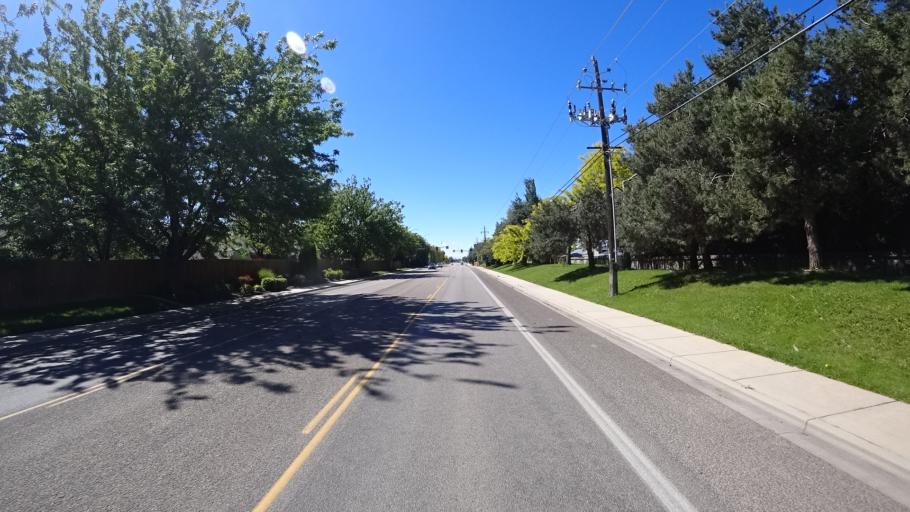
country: US
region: Idaho
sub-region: Ada County
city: Meridian
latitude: 43.6260
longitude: -116.3746
